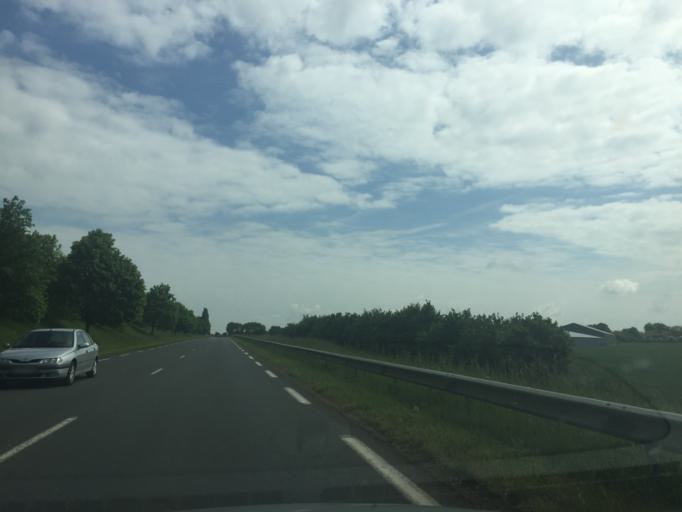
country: FR
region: Poitou-Charentes
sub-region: Departement de la Vienne
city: Lusignan
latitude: 46.4309
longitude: 0.1318
